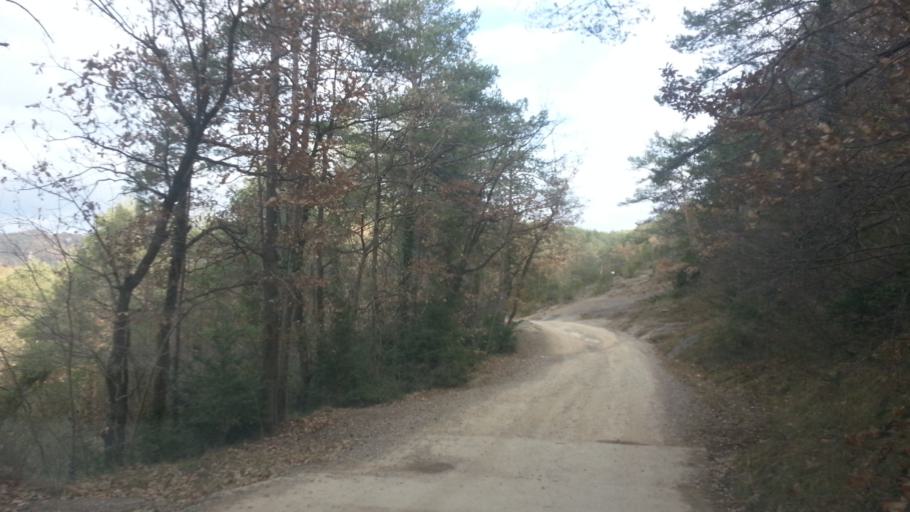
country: ES
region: Catalonia
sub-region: Provincia de Barcelona
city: Alpens
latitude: 42.1343
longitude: 2.0494
